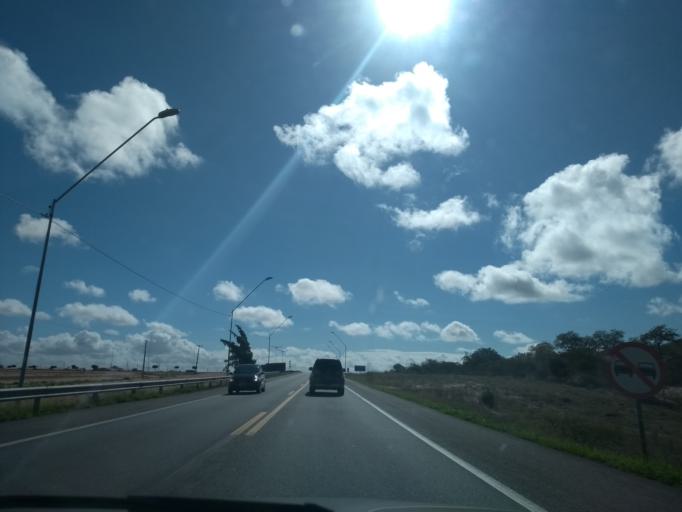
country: BR
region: Bahia
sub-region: Amargosa
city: Amargosa
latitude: -12.8622
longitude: -39.8521
